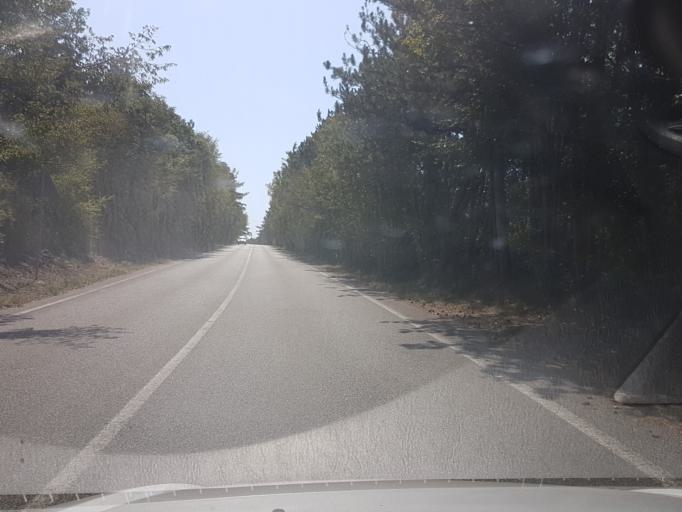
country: IT
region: Friuli Venezia Giulia
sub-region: Provincia di Trieste
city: Aurisina
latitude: 45.7673
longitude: 13.6953
